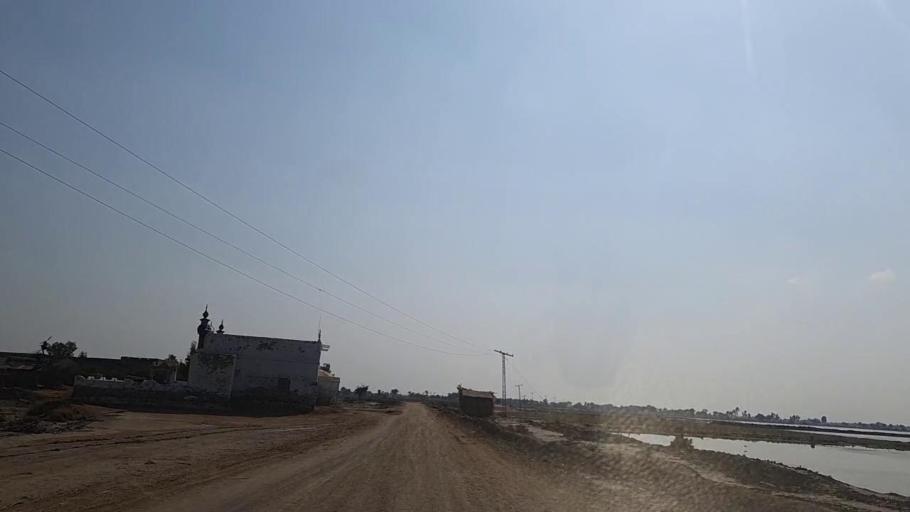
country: PK
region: Sindh
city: Daur
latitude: 26.4597
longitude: 68.2505
